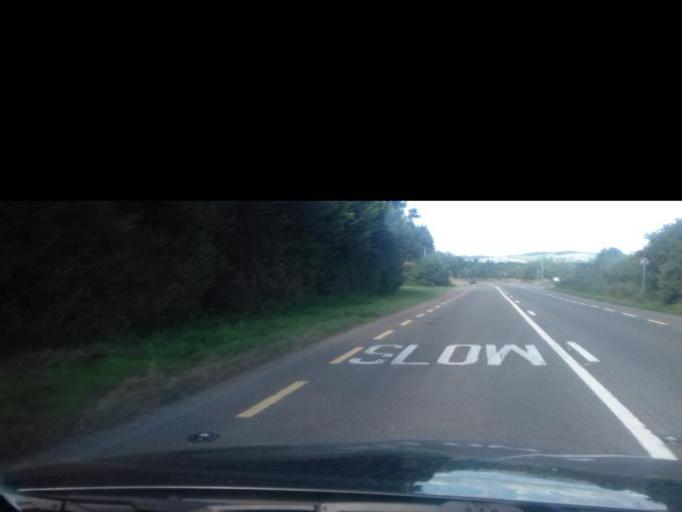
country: IE
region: Munster
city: Carrick-on-Suir
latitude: 52.4290
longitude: -7.4688
